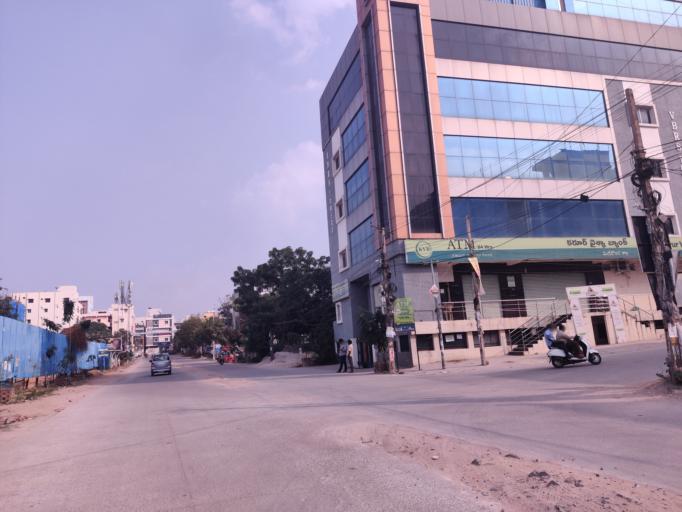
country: IN
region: Telangana
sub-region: Hyderabad
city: Hyderabad
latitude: 17.4034
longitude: 78.3891
